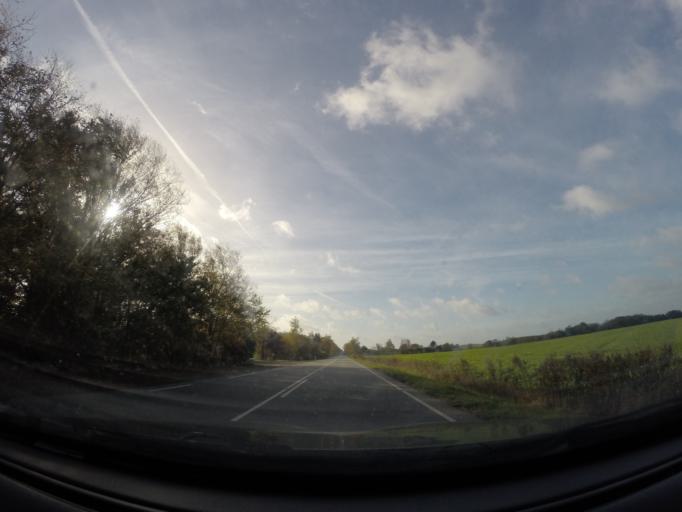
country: DK
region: South Denmark
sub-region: Faaborg-Midtfyn Kommune
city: Ringe
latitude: 55.2025
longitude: 10.5616
